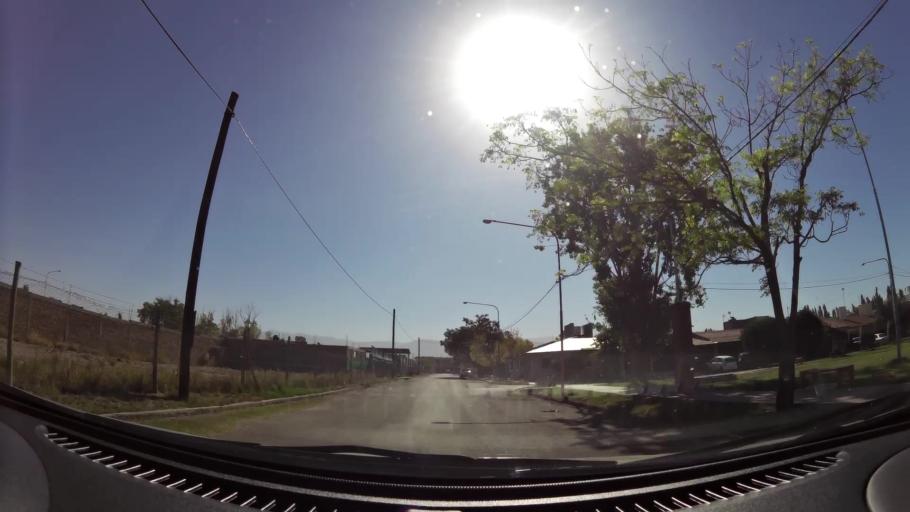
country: AR
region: Mendoza
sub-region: Departamento de Godoy Cruz
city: Godoy Cruz
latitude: -32.9230
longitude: -68.8024
